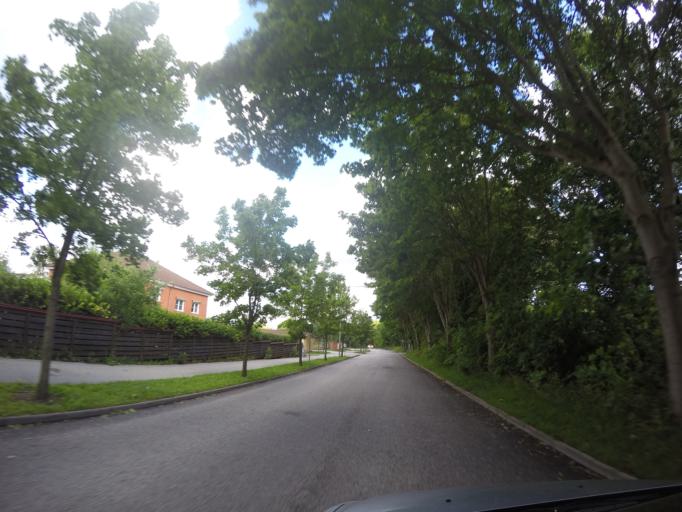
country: SE
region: Skane
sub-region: Lunds Kommun
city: Lund
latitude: 55.6991
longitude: 13.2462
